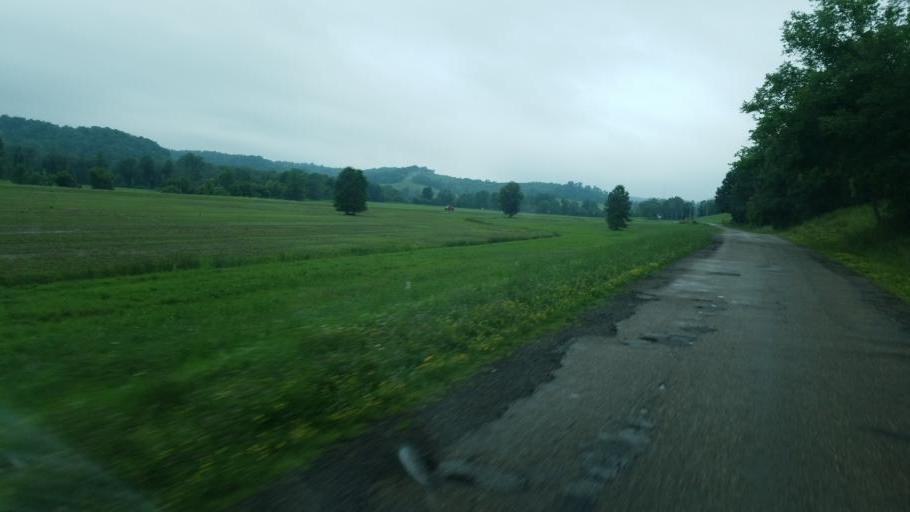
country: US
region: Ohio
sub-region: Tuscarawas County
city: Dennison
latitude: 40.3801
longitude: -81.2503
